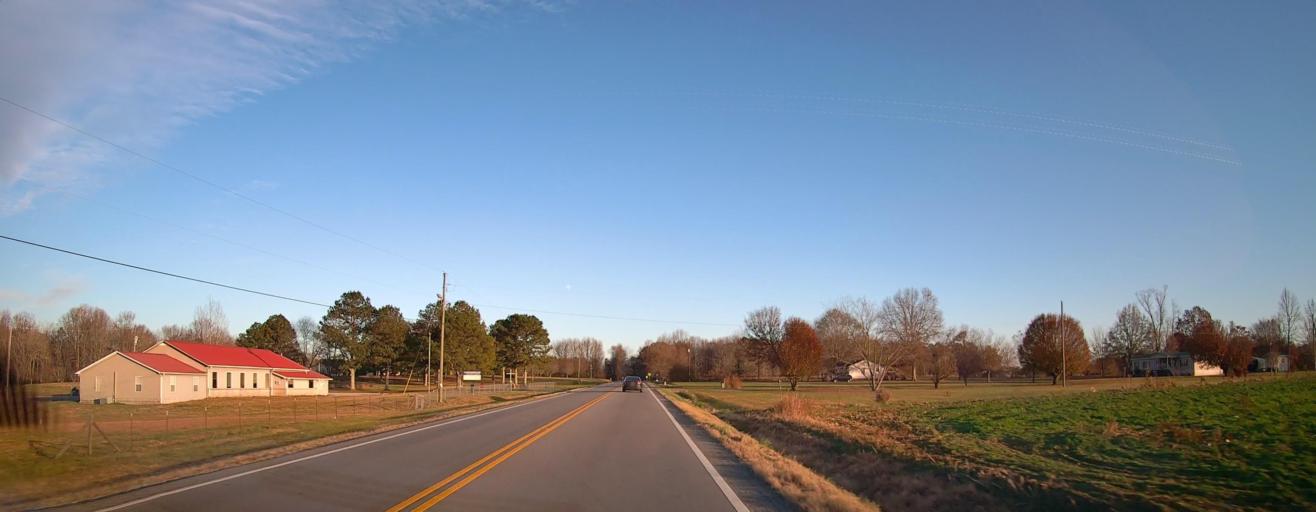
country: US
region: Alabama
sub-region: Saint Clair County
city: Steele
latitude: 34.0622
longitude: -86.2396
